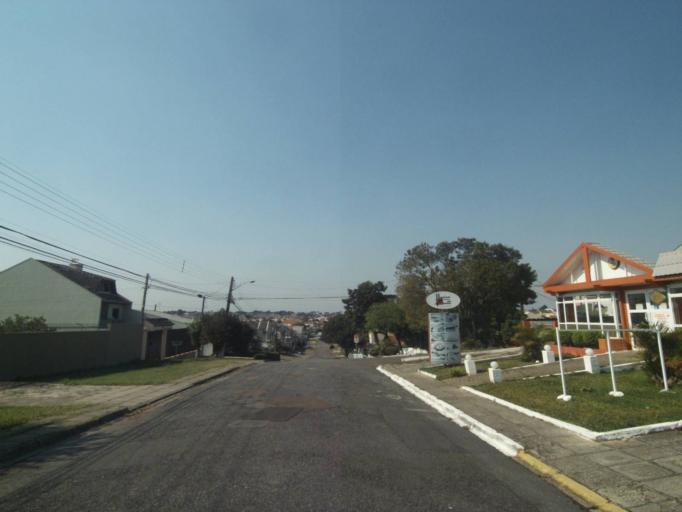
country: BR
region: Parana
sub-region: Sao Jose Dos Pinhais
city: Sao Jose dos Pinhais
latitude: -25.4951
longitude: -49.2623
